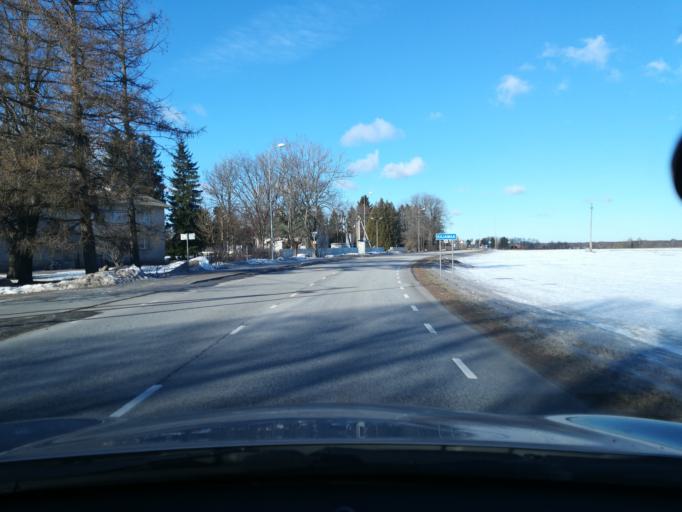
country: EE
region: Harju
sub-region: Saku vald
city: Saku
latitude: 59.2740
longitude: 24.7203
